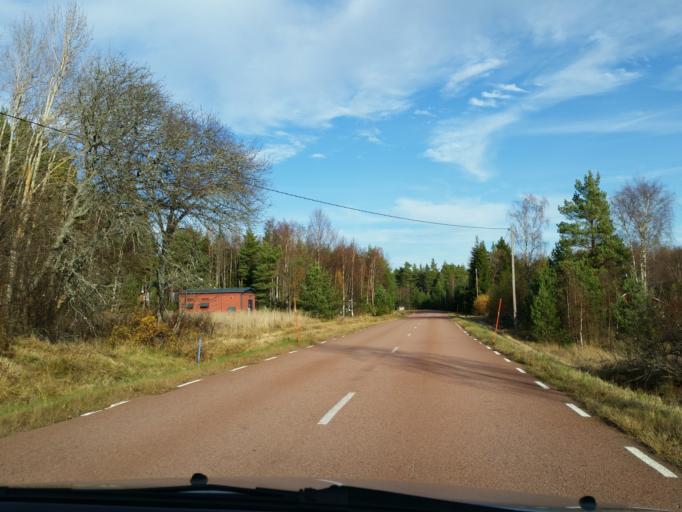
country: AX
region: Alands landsbygd
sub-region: Saltvik
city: Saltvik
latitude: 60.3488
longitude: 20.0938
